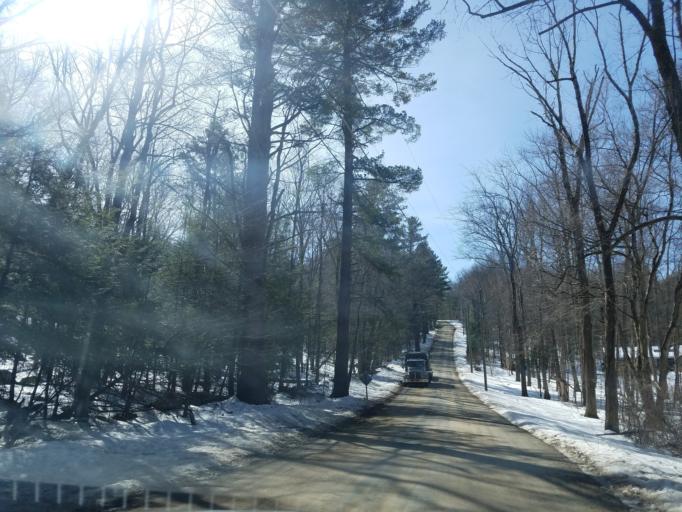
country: US
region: Connecticut
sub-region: Litchfield County
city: Canaan
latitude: 41.8672
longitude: -73.3523
